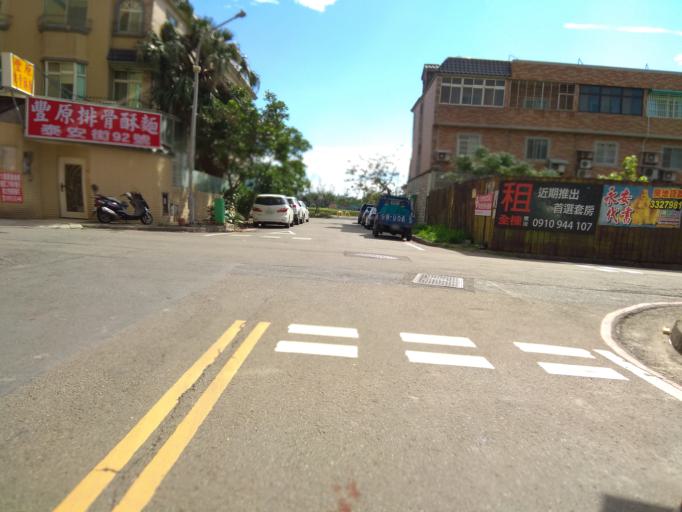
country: TW
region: Taiwan
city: Taoyuan City
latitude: 25.0490
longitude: 121.1204
